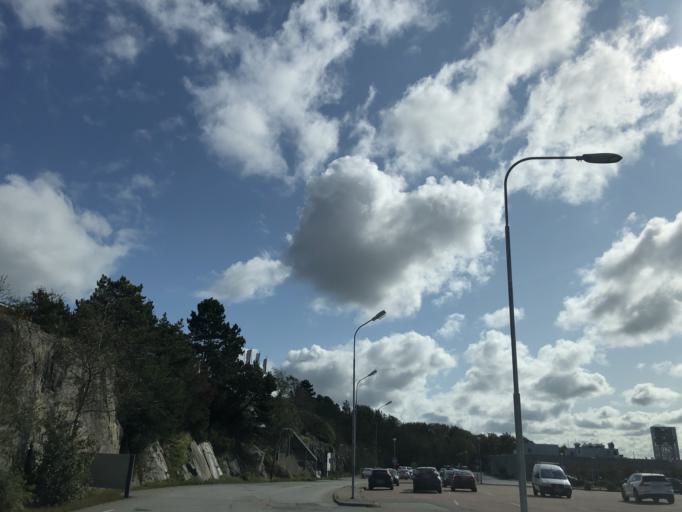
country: SE
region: Vaestra Goetaland
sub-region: Goteborg
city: Majorna
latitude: 57.7208
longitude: 11.8493
